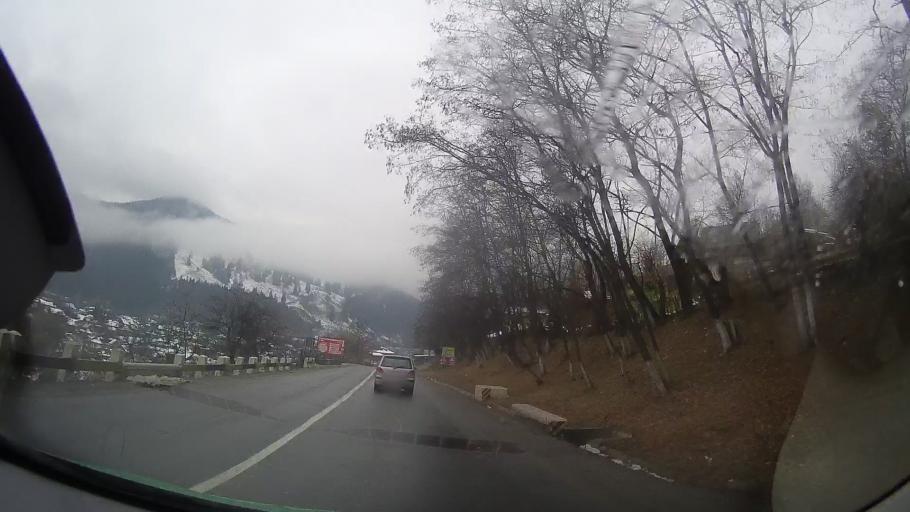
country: RO
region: Neamt
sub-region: Comuna Bicaz
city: Dodeni
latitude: 46.9026
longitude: 26.1145
